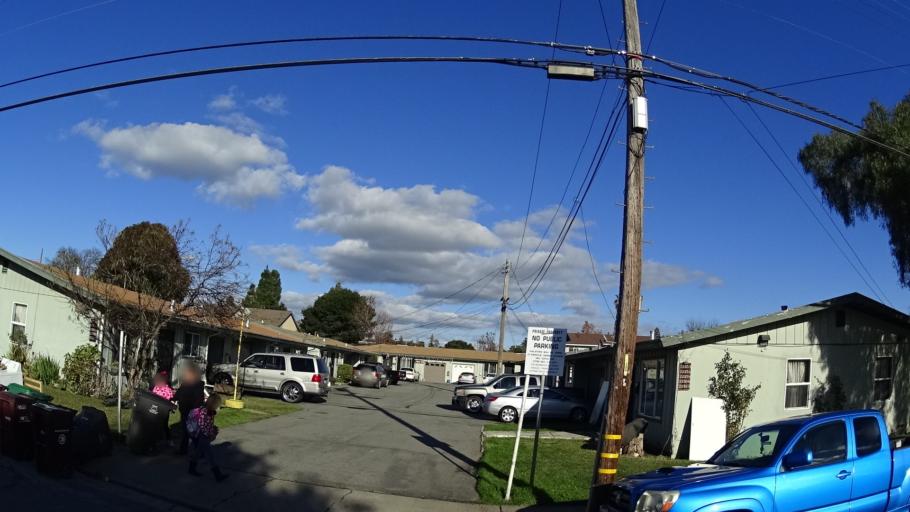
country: US
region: California
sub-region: Alameda County
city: Cherryland
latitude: 37.6716
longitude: -122.0937
